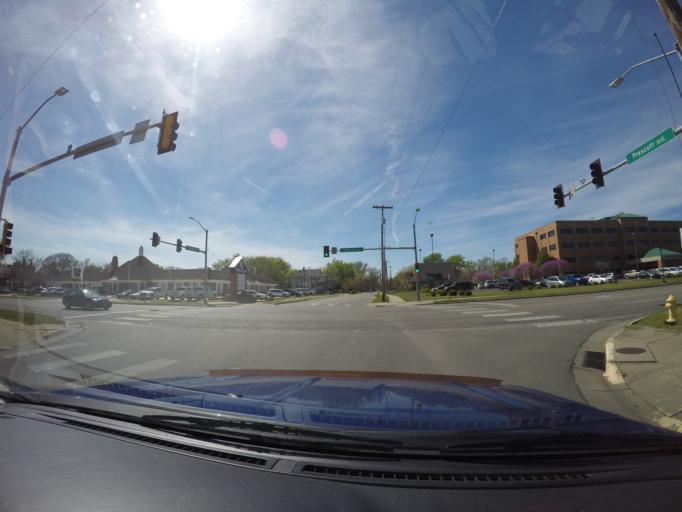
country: US
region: Kansas
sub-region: Saline County
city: Salina
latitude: 38.8304
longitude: -97.6090
